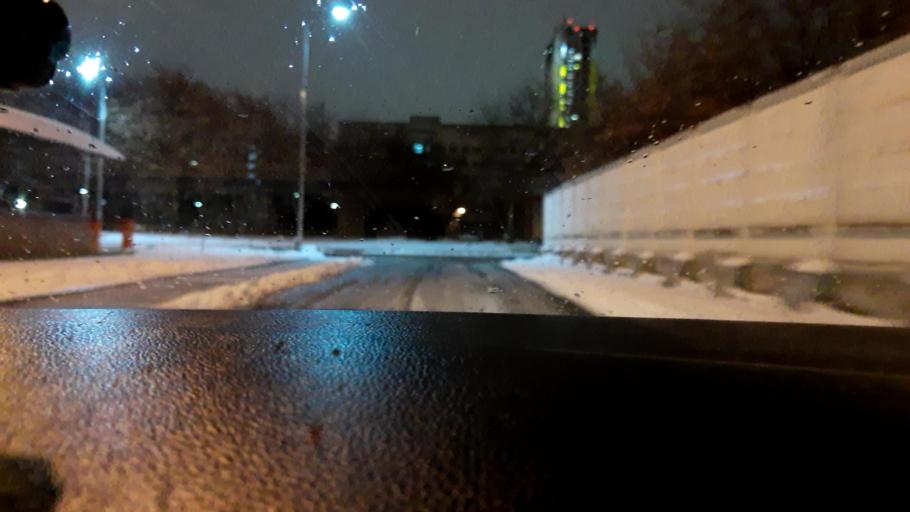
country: RU
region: Moscow
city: Vatutino
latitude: 55.8563
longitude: 37.6963
